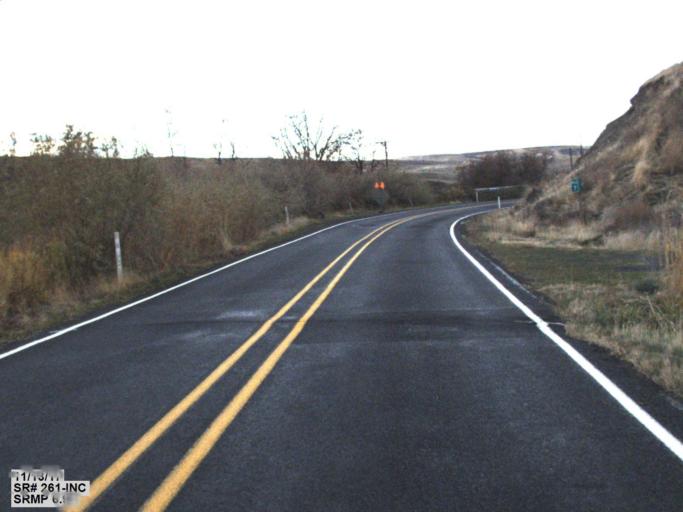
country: US
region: Washington
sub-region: Columbia County
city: Dayton
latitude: 46.5127
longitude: -118.1083
